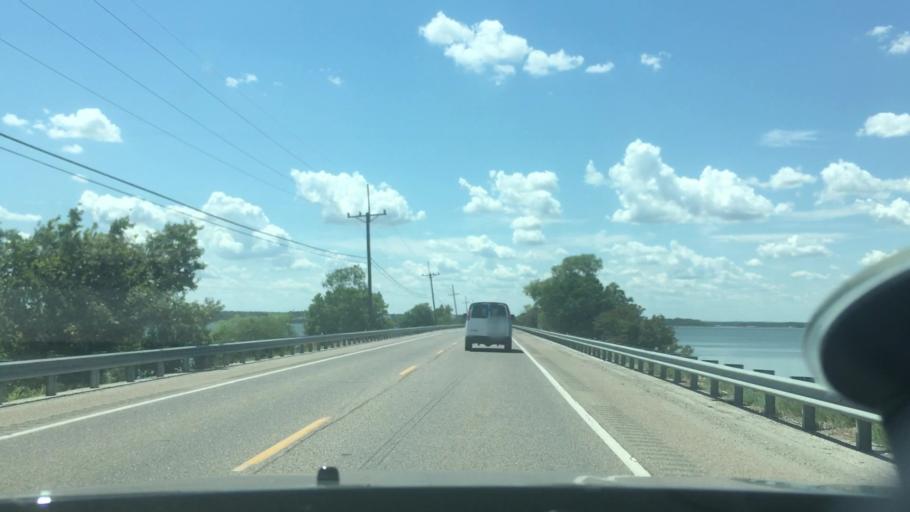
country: US
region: Oklahoma
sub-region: Marshall County
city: Kingston
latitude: 34.0009
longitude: -96.6046
